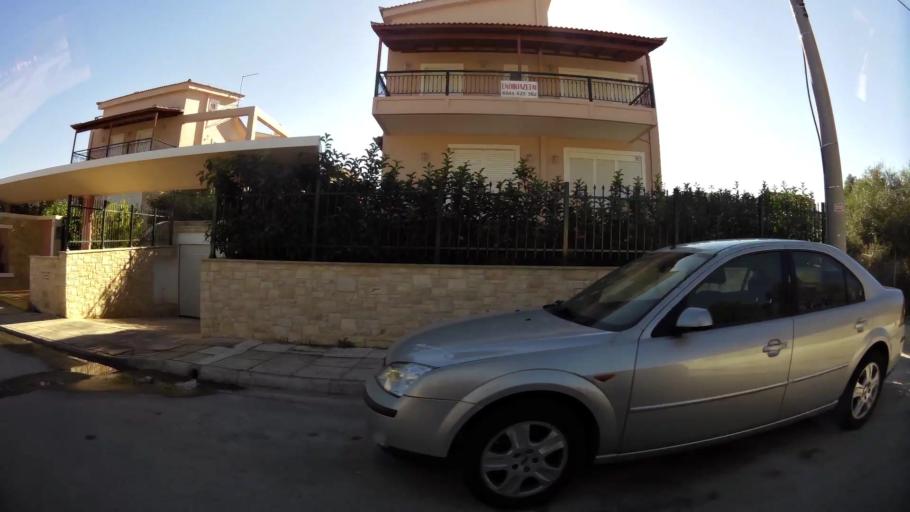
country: GR
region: Attica
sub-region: Nomarchia Anatolikis Attikis
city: Kalyvia Thorikou
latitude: 37.8359
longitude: 23.9322
